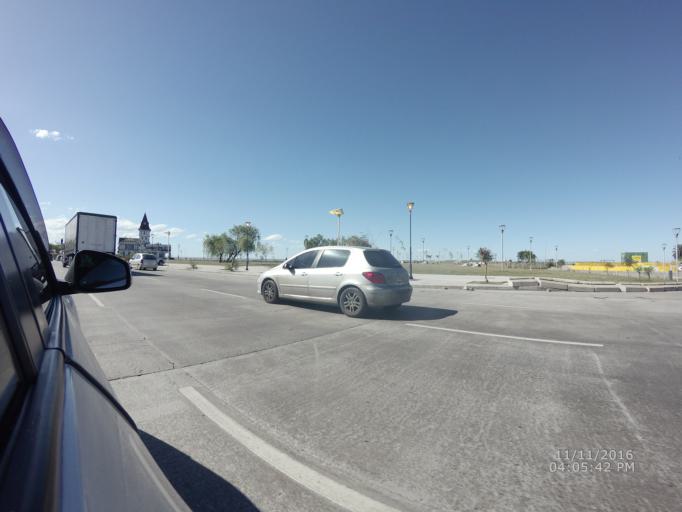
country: AR
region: Buenos Aires F.D.
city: Retiro
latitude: -34.5648
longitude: -58.4025
